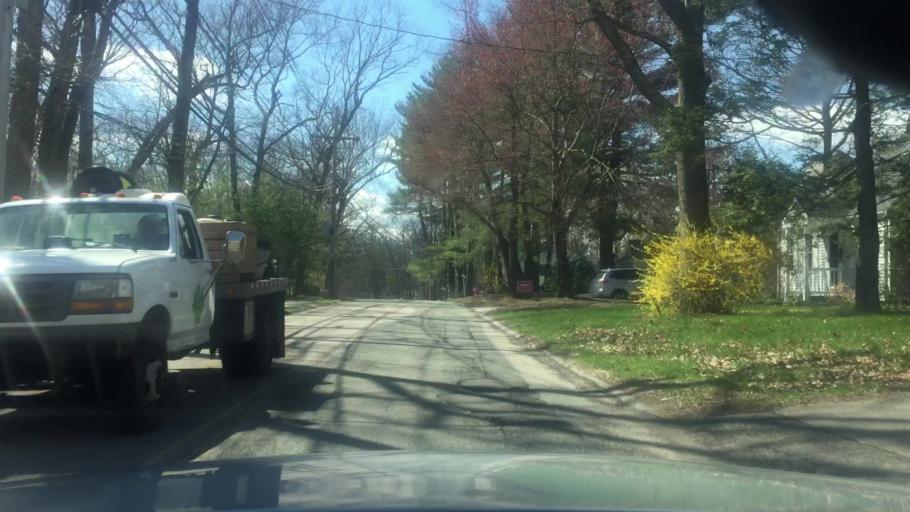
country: US
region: Massachusetts
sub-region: Norfolk County
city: Needham
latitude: 42.2759
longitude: -71.2536
